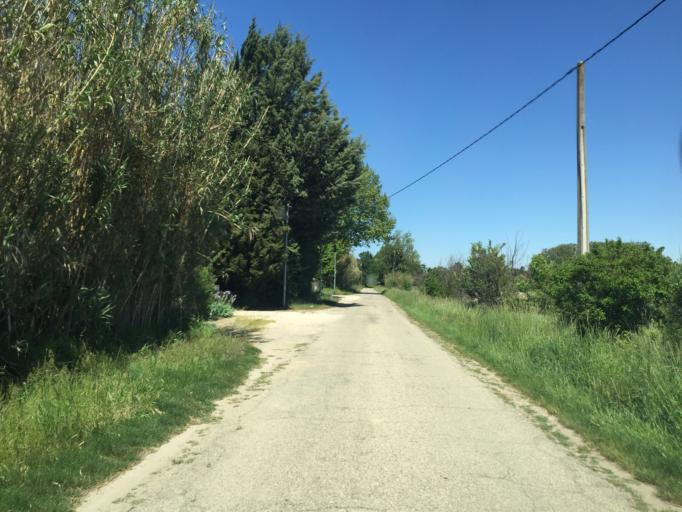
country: FR
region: Provence-Alpes-Cote d'Azur
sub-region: Departement du Vaucluse
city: Jonquieres
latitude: 44.1293
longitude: 4.9083
